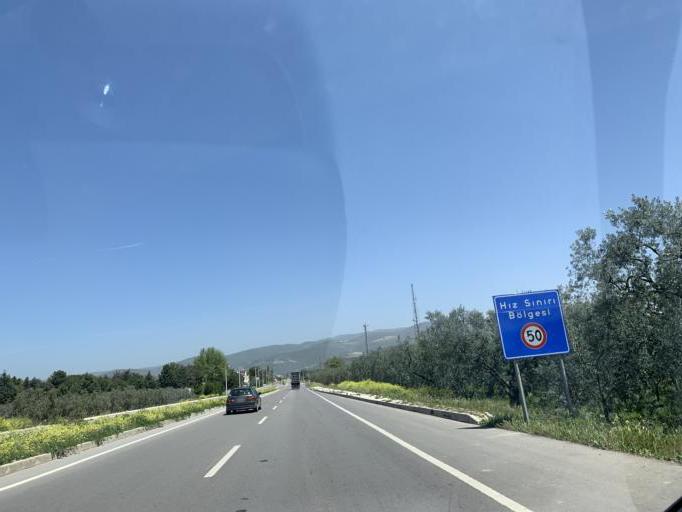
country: TR
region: Bursa
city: Iznik
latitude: 40.4040
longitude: 29.7008
